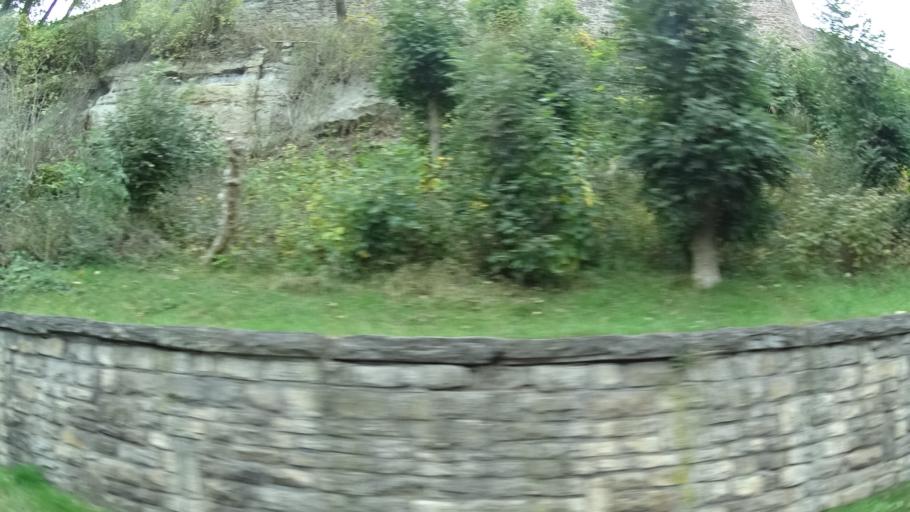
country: DE
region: Thuringia
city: Walldorf
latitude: 50.6131
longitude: 10.3887
